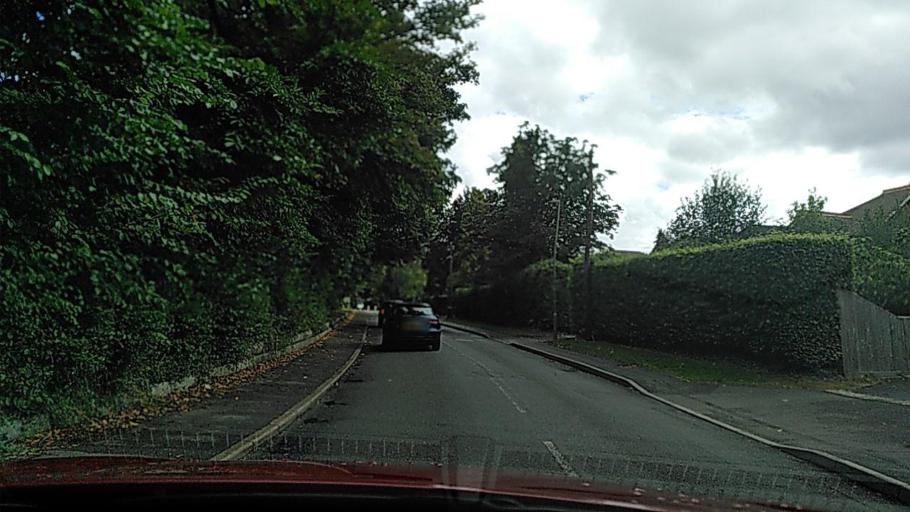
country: GB
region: England
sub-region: Oxfordshire
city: Henley on Thames
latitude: 51.5294
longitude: -0.9192
